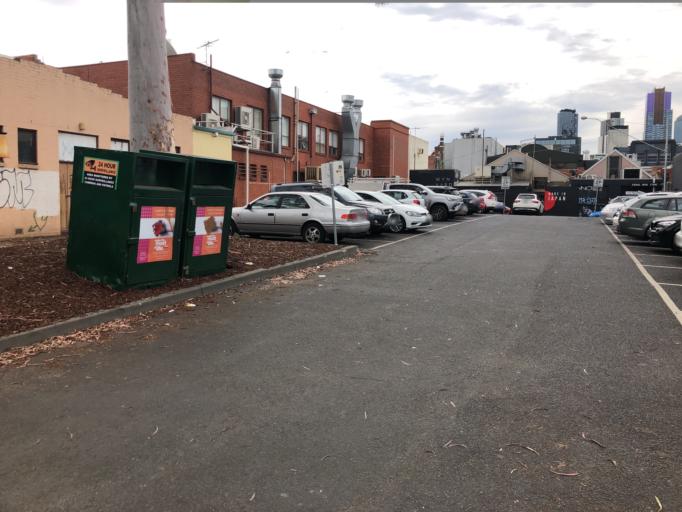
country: AU
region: Victoria
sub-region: Port Phillip
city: South Melbourne
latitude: -37.8348
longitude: 144.9621
